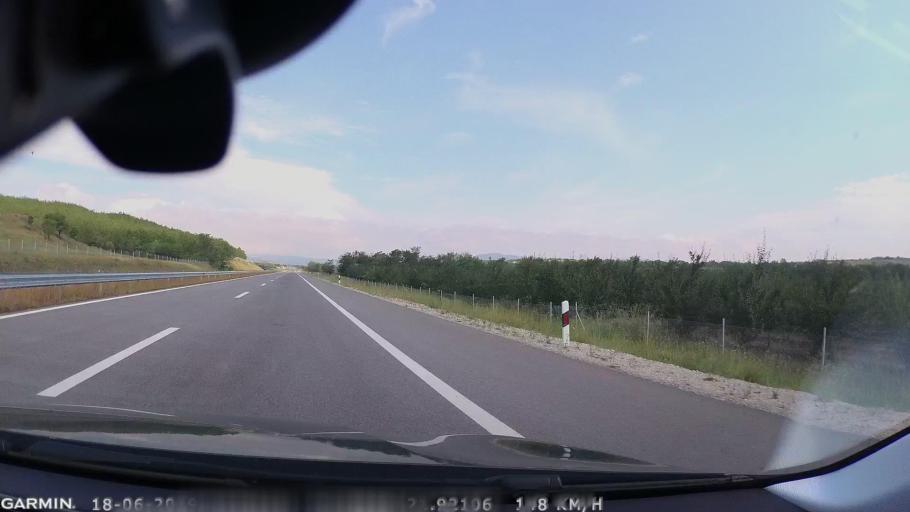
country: MK
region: Sveti Nikole
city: Sveti Nikole
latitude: 41.8979
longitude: 21.9191
